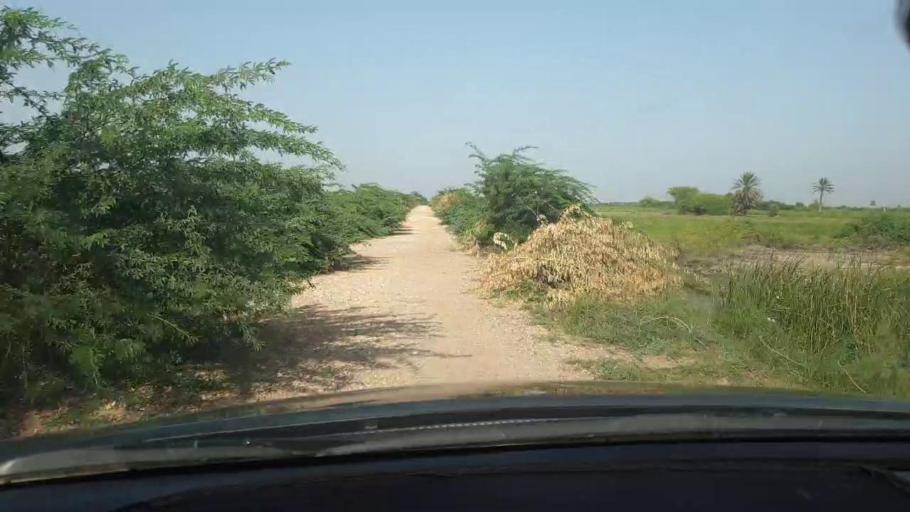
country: PK
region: Sindh
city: Tando Bago
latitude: 24.6800
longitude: 69.1584
